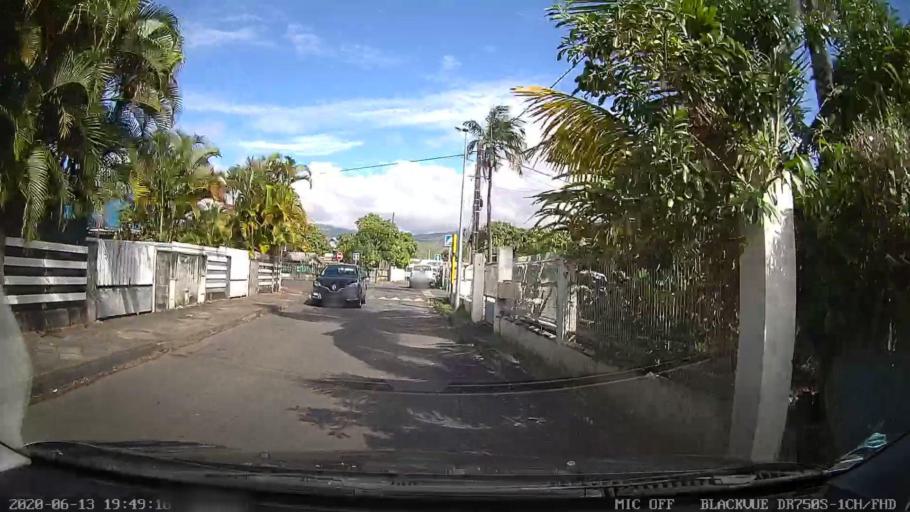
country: RE
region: Reunion
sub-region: Reunion
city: Bras-Panon
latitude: -21.0043
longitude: 55.6892
